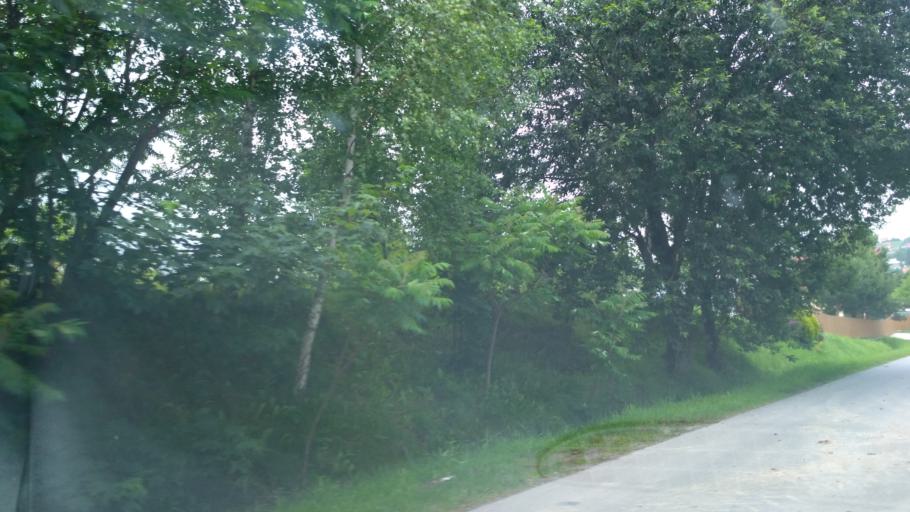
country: PL
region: Subcarpathian Voivodeship
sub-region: Powiat jaroslawski
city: Pruchnik
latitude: 49.8985
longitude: 22.5179
